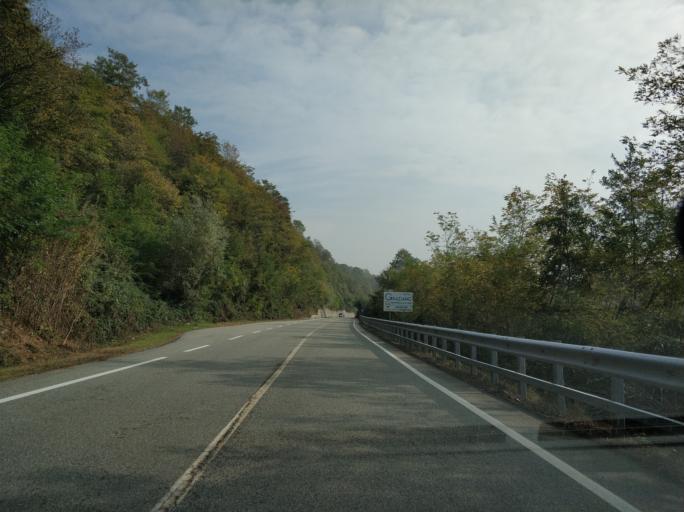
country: IT
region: Piedmont
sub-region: Provincia di Biella
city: Netro
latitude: 45.5217
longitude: 7.9371
